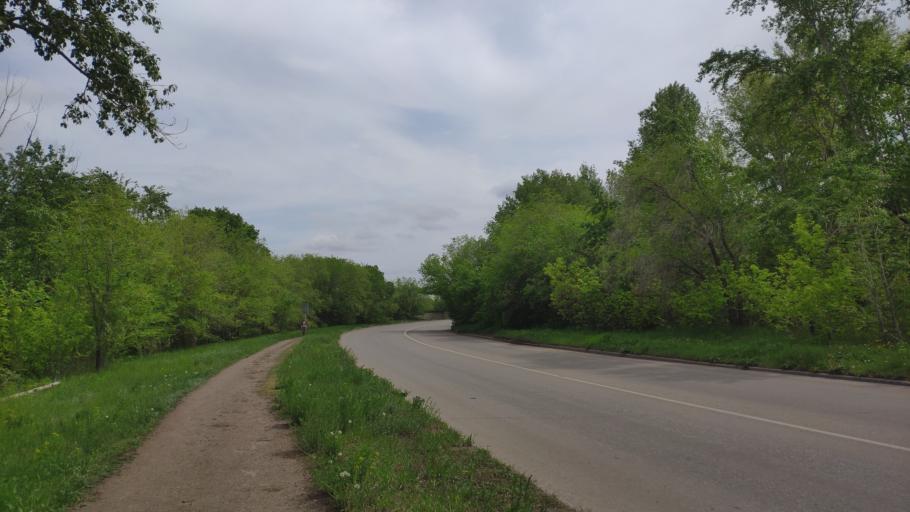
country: RU
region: Chelyabinsk
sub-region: Gorod Magnitogorsk
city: Magnitogorsk
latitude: 53.4164
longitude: 58.9552
